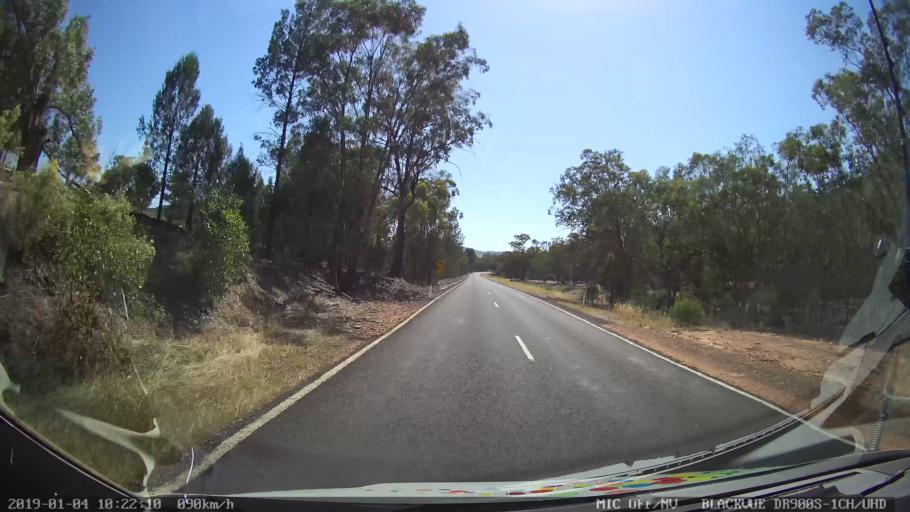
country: AU
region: New South Wales
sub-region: Cabonne
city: Canowindra
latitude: -33.3689
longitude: 148.5211
